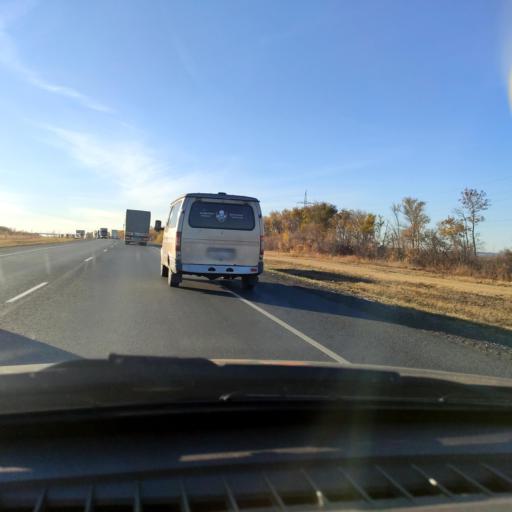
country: RU
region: Samara
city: Varlamovo
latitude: 53.1964
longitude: 48.3110
